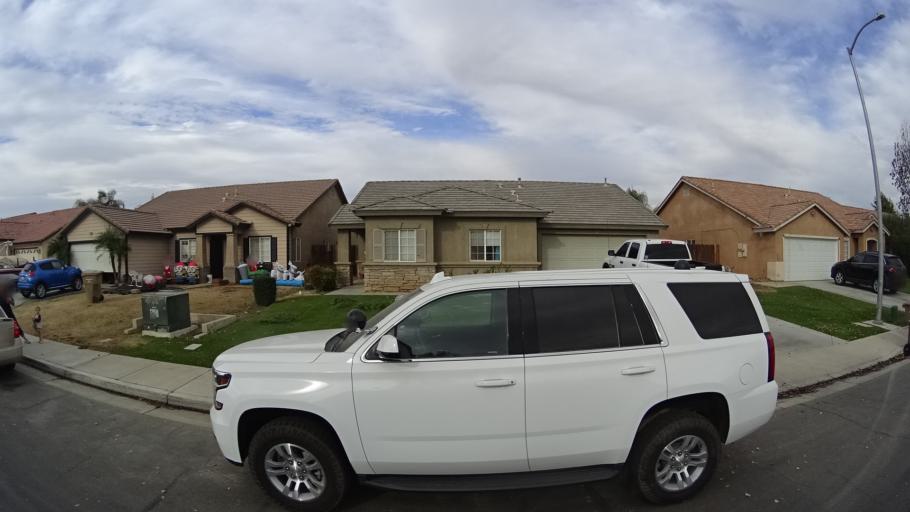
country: US
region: California
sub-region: Kern County
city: Rosedale
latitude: 35.4191
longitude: -119.1347
